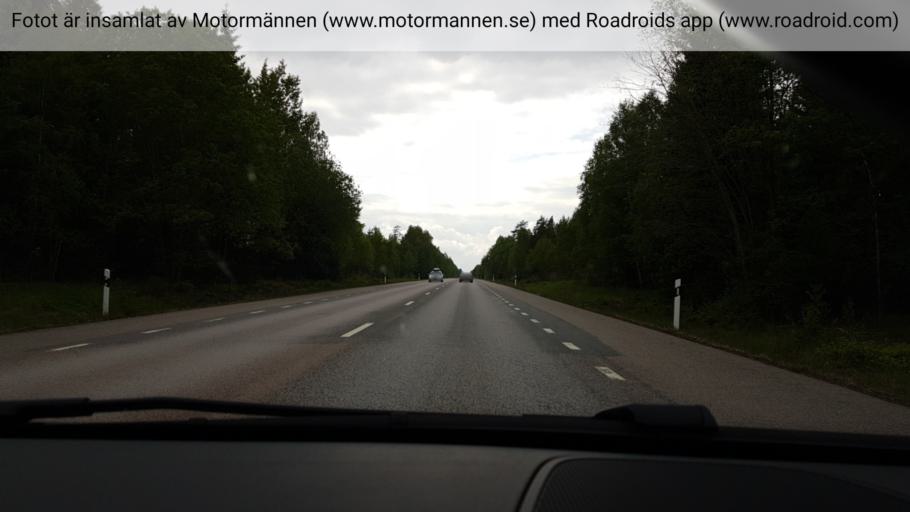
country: SE
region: Uppsala
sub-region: Osthammars Kommun
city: Gimo
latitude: 60.1646
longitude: 18.1176
